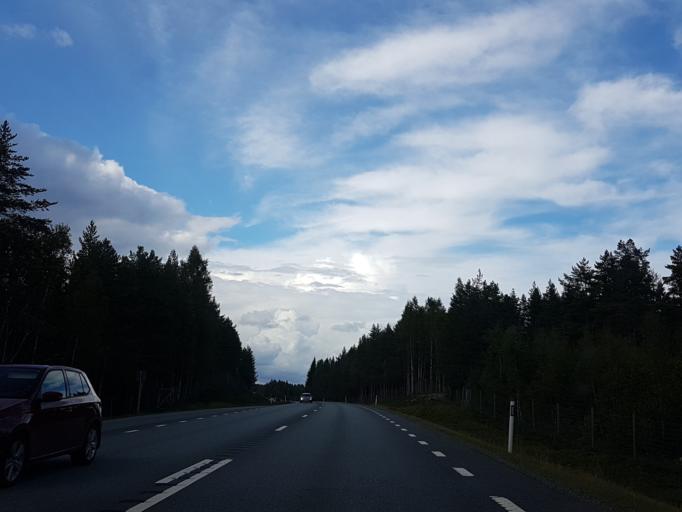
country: SE
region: Vaesterbotten
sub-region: Robertsfors Kommun
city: Robertsfors
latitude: 64.0242
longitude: 20.8408
